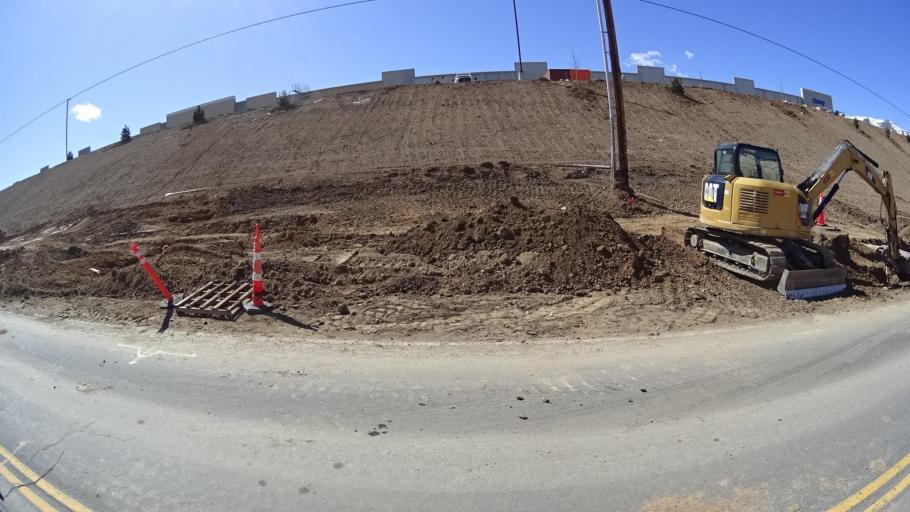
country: US
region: Nevada
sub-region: Washoe County
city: Golden Valley
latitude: 39.6029
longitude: -119.8508
